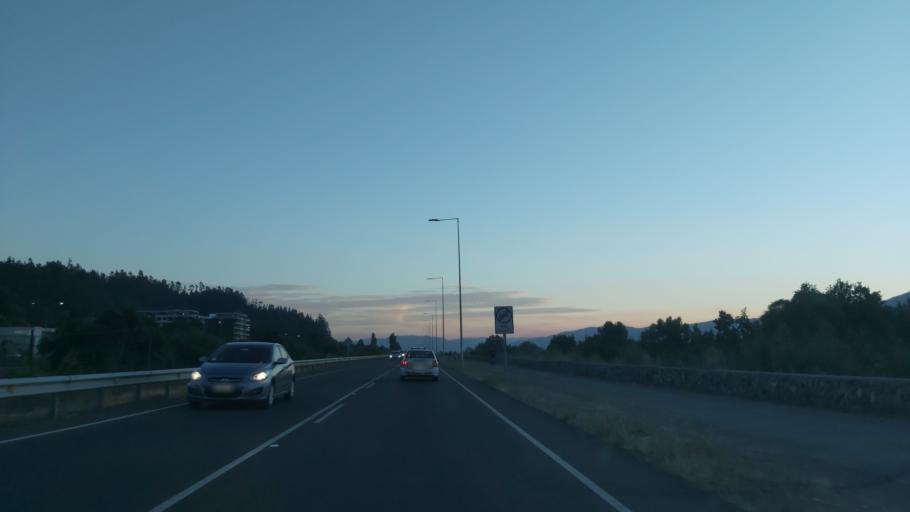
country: CL
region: Biobio
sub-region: Provincia de Concepcion
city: Chiguayante
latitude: -36.8791
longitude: -73.0390
